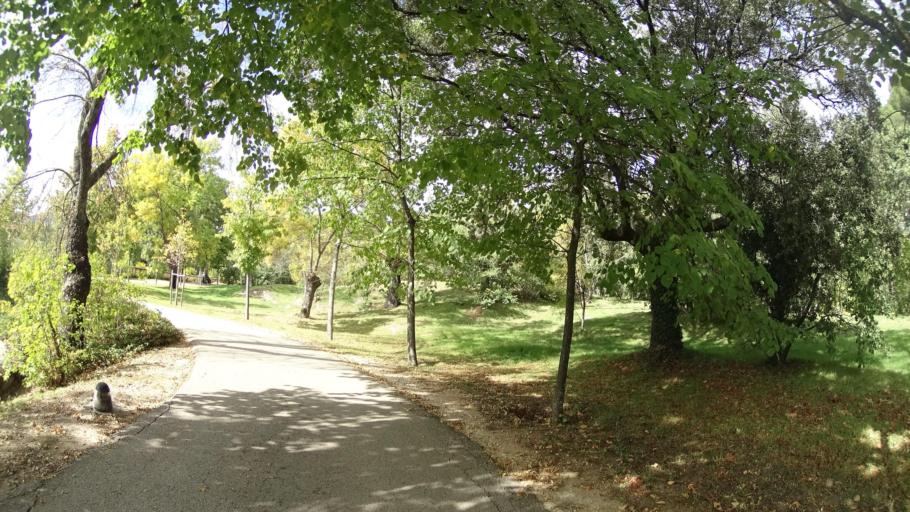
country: ES
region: Madrid
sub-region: Provincia de Madrid
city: El Escorial
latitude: 40.5849
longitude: -4.1376
